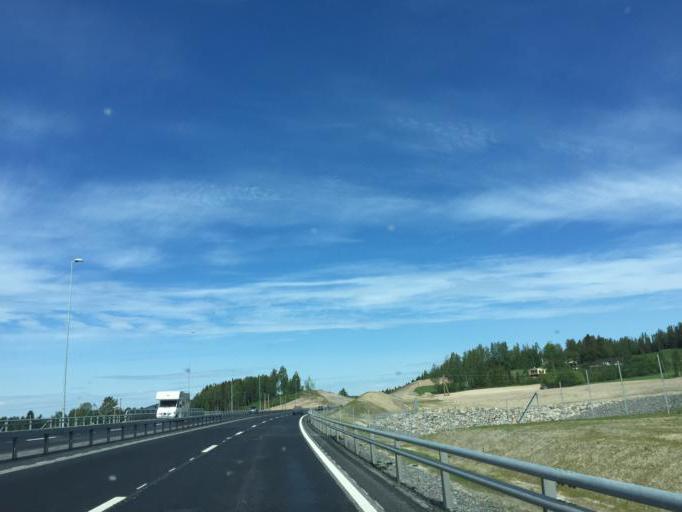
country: NO
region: Hedmark
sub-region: Kongsvinger
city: Spetalen
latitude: 60.2170
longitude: 11.8685
